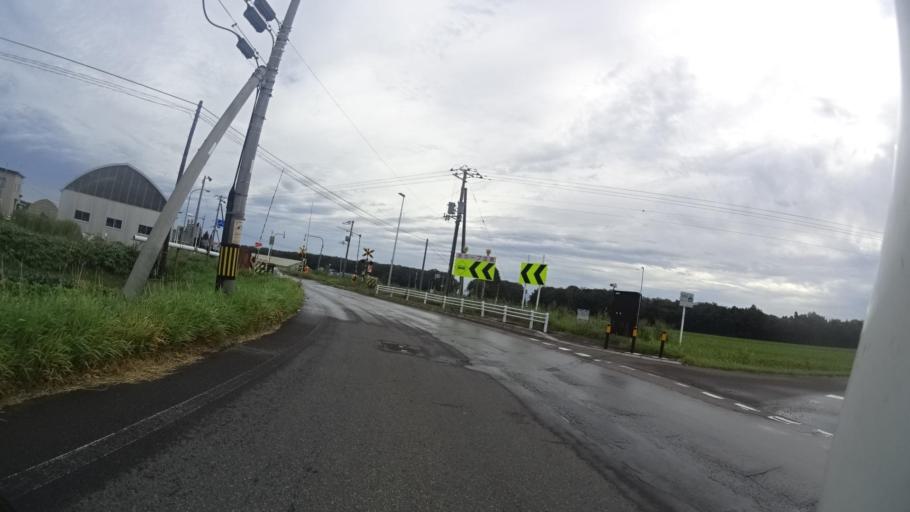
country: JP
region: Hokkaido
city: Abashiri
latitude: 43.8599
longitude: 144.6148
